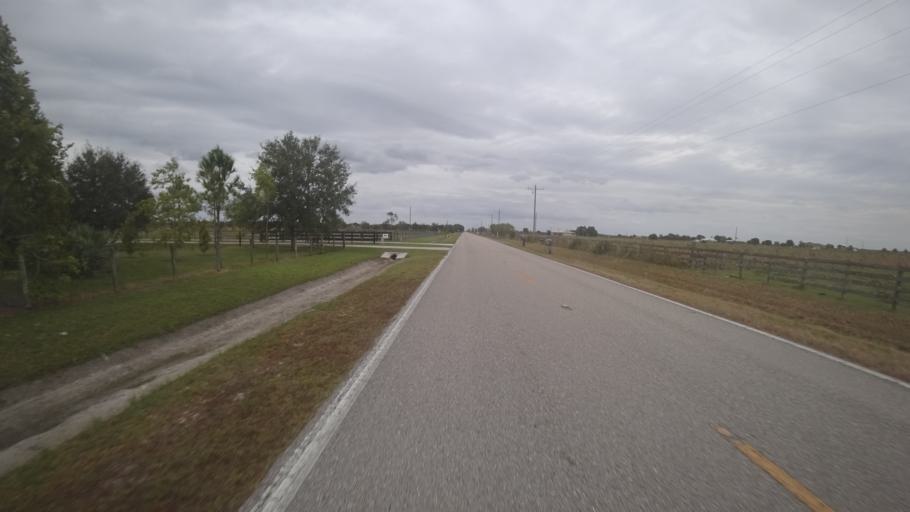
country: US
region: Florida
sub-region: Sarasota County
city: Warm Mineral Springs
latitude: 27.2817
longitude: -82.1942
